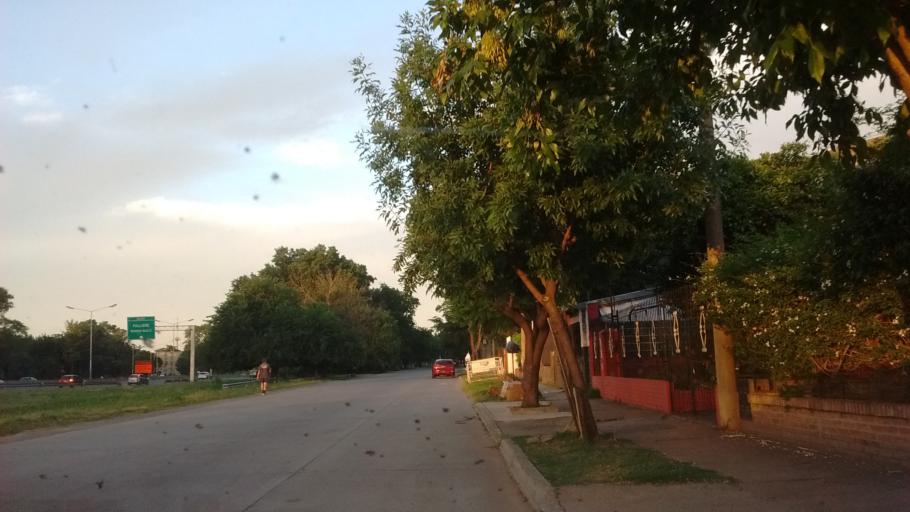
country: AR
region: Santa Fe
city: Granadero Baigorria
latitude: -32.8908
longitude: -60.7167
